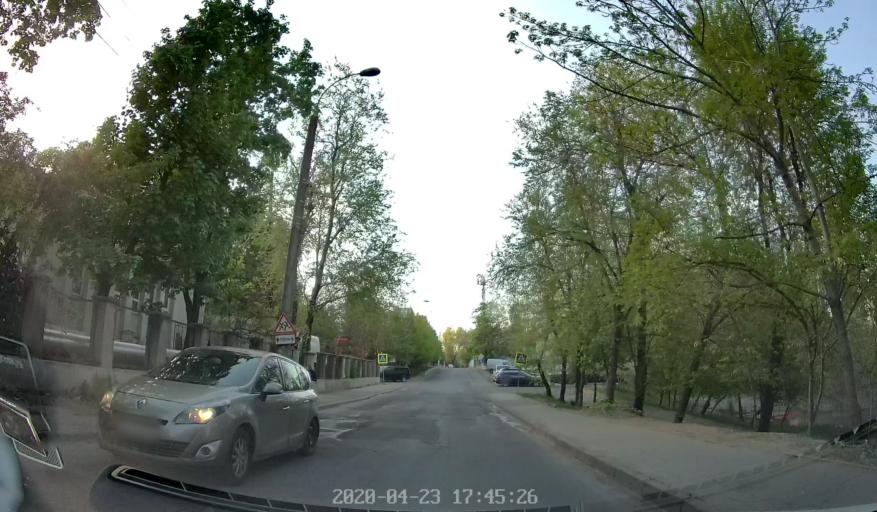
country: MD
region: Chisinau
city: Chisinau
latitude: 46.9957
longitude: 28.8251
